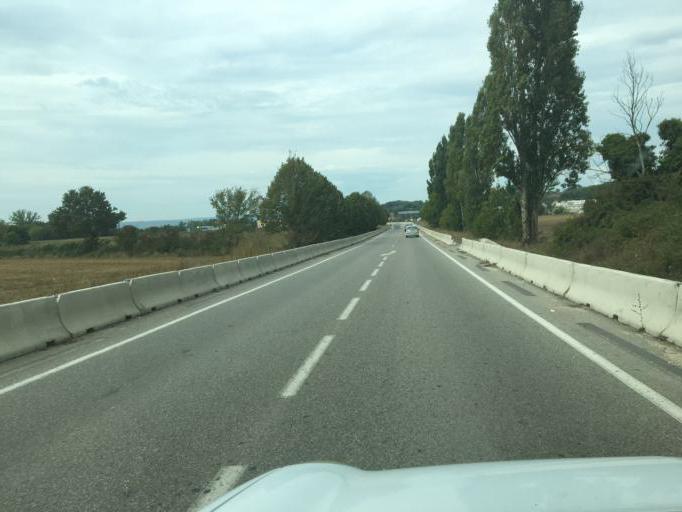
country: FR
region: Provence-Alpes-Cote d'Azur
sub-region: Departement des Bouches-du-Rhone
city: Bouc-Bel-Air
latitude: 43.4746
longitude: 5.3984
